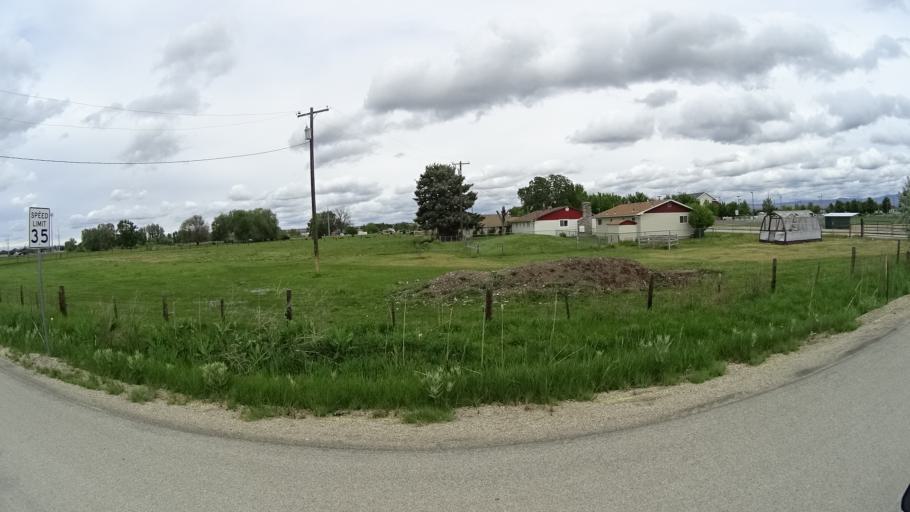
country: US
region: Idaho
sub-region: Ada County
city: Star
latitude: 43.6890
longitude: -116.4514
